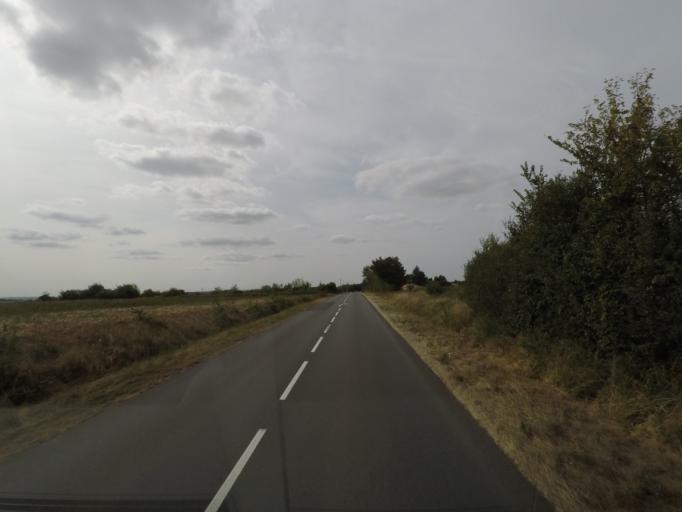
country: FR
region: Poitou-Charentes
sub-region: Departement de la Charente
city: Nanteuil-en-Vallee
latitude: 45.9884
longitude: 0.3390
